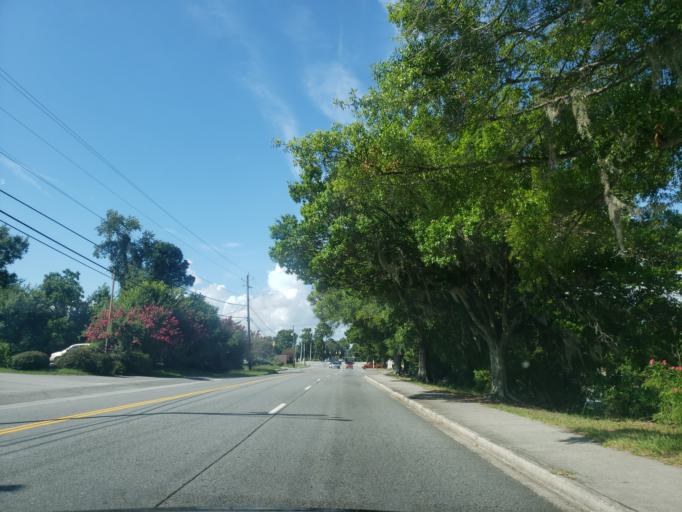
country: US
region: Georgia
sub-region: Chatham County
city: Georgetown
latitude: 31.9835
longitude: -81.1682
